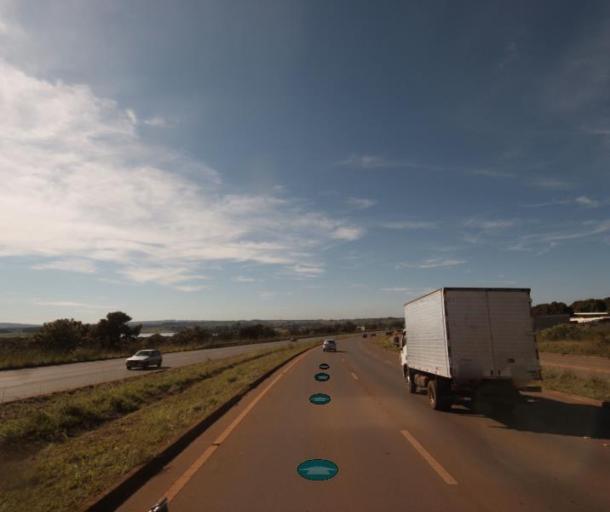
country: BR
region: Federal District
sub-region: Brasilia
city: Brasilia
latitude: -15.7635
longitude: -48.2325
